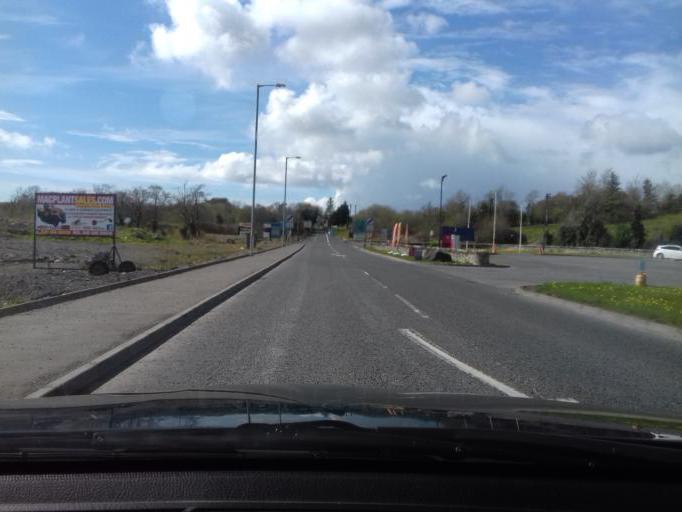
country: IE
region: Ulster
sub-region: County Donegal
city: Ballyshannon
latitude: 54.4769
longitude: -8.0968
